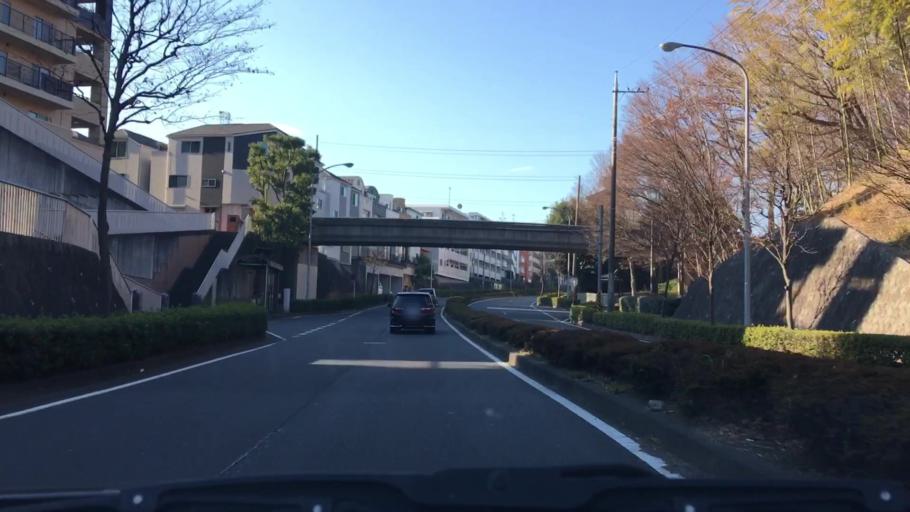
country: JP
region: Tokyo
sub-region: Machida-shi
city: Machida
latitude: 35.5498
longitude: 139.5599
